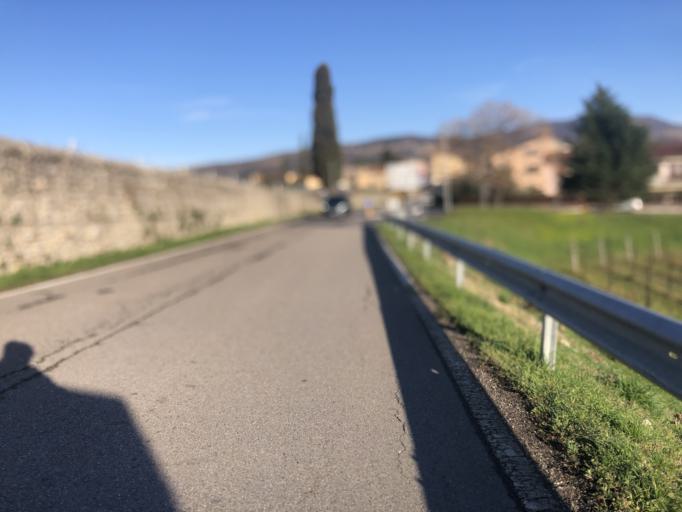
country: IT
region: Veneto
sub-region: Provincia di Verona
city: San Pietro in Cariano
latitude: 45.5140
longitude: 10.8882
